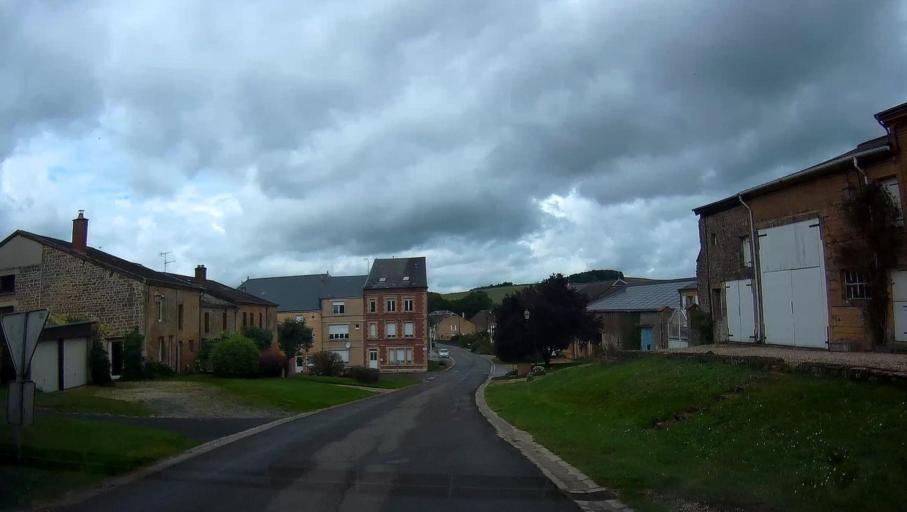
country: FR
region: Champagne-Ardenne
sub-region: Departement des Ardennes
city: Rimogne
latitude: 49.7540
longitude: 4.5570
